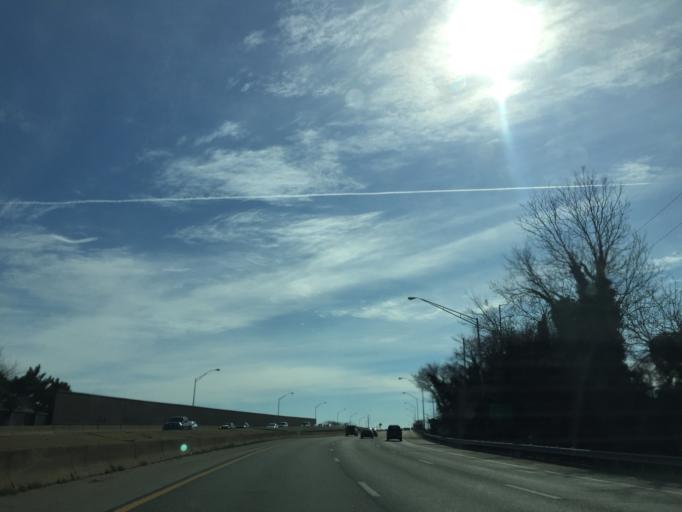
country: US
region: Virginia
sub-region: City of Hampton
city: Hampton
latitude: 37.0330
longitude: -76.3406
